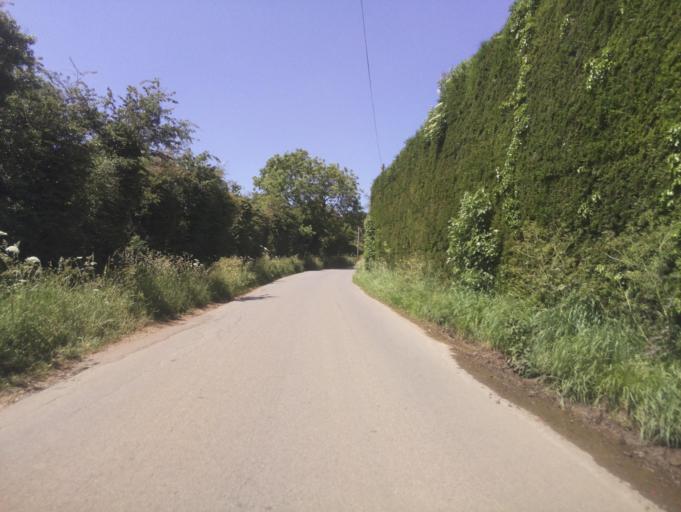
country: GB
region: England
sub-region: Wiltshire
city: Bremhill
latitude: 51.4526
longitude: -2.0351
